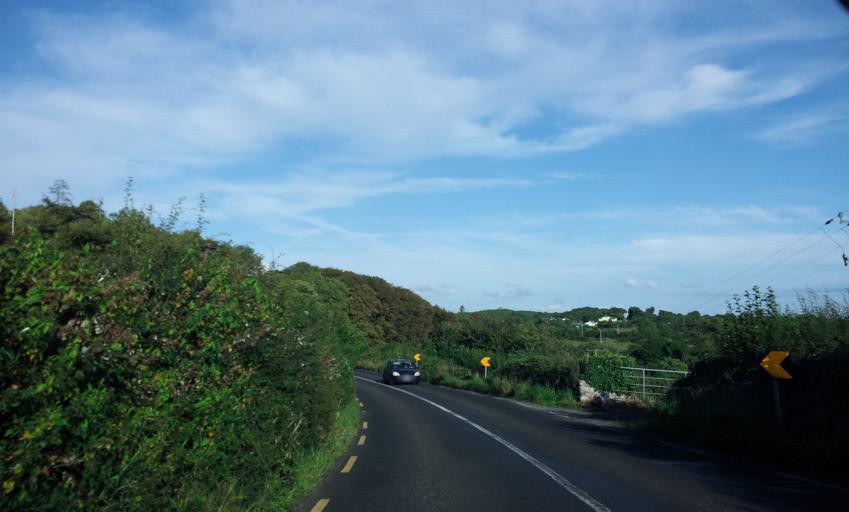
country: IE
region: Munster
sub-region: An Clar
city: Ennis
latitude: 52.9770
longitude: -9.1093
